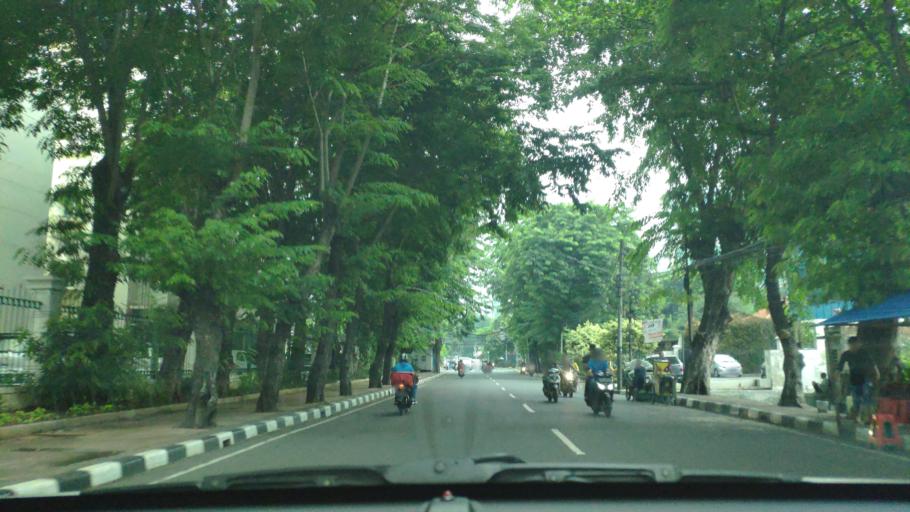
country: ID
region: Jakarta Raya
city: Jakarta
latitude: -6.1743
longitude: 106.8158
